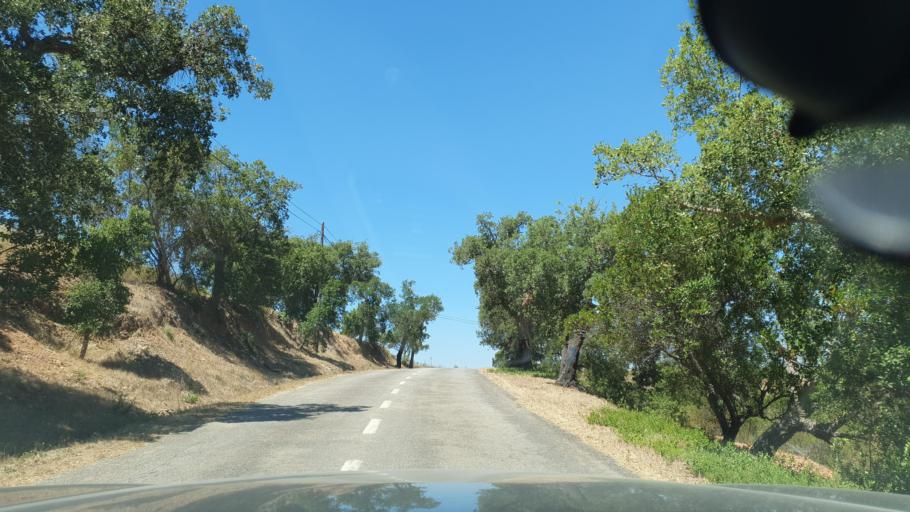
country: PT
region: Beja
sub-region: Odemira
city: Odemira
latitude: 37.6105
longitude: -8.5014
